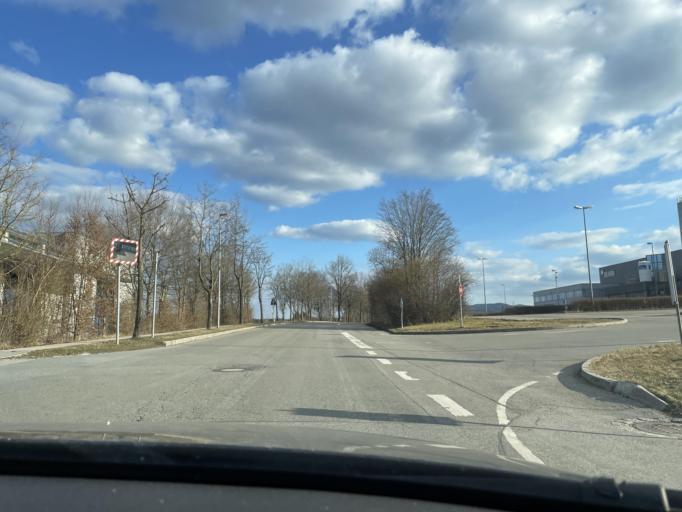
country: DE
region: Bavaria
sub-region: Lower Bavaria
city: Viechtach
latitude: 49.0694
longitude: 12.8822
